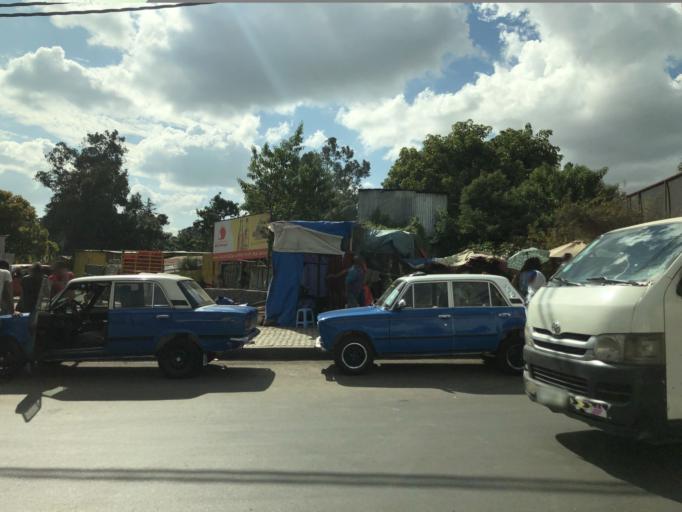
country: ET
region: Adis Abeba
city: Addis Ababa
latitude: 9.0321
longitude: 38.7735
